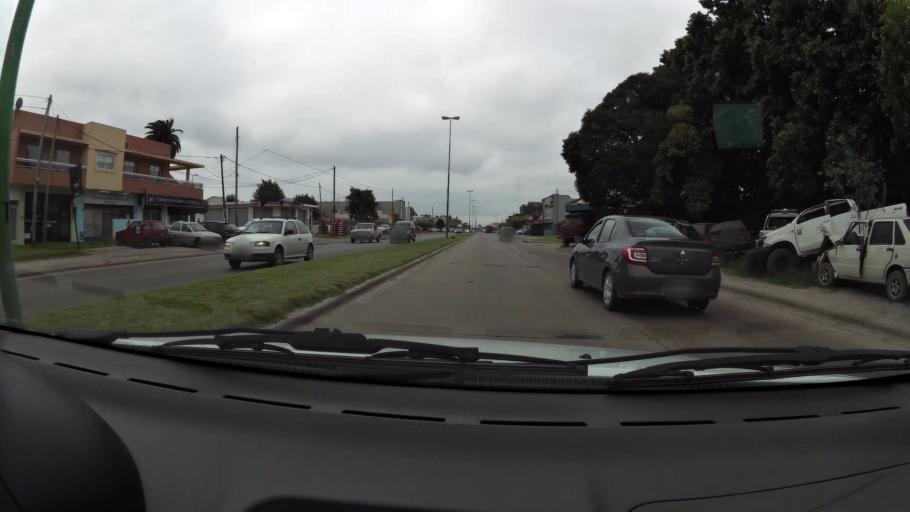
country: AR
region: Buenos Aires
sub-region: Partido de La Plata
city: La Plata
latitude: -35.0001
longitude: -58.0536
